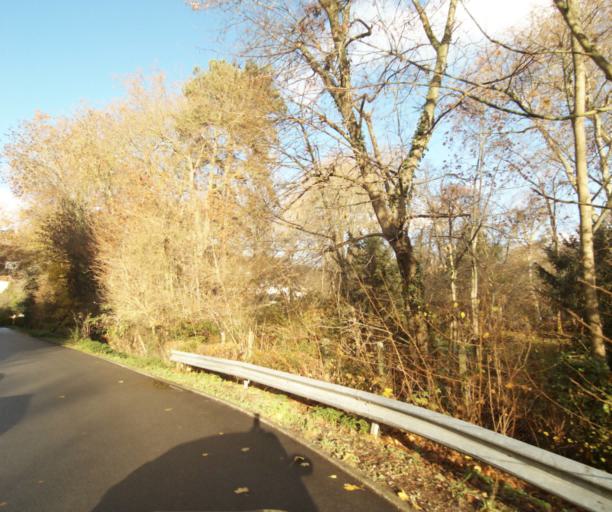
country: FR
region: Ile-de-France
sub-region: Departement des Yvelines
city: Meulan-en-Yvelines
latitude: 49.0041
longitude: 1.9163
